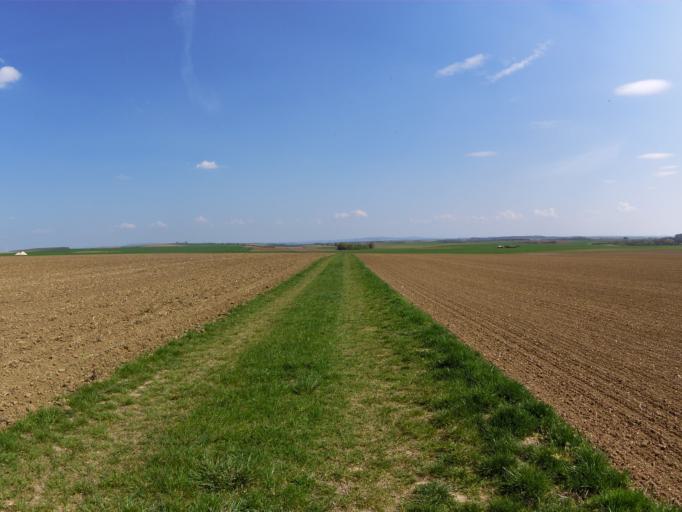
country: DE
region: Bavaria
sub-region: Regierungsbezirk Unterfranken
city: Giebelstadt
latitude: 49.6818
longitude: 9.9593
